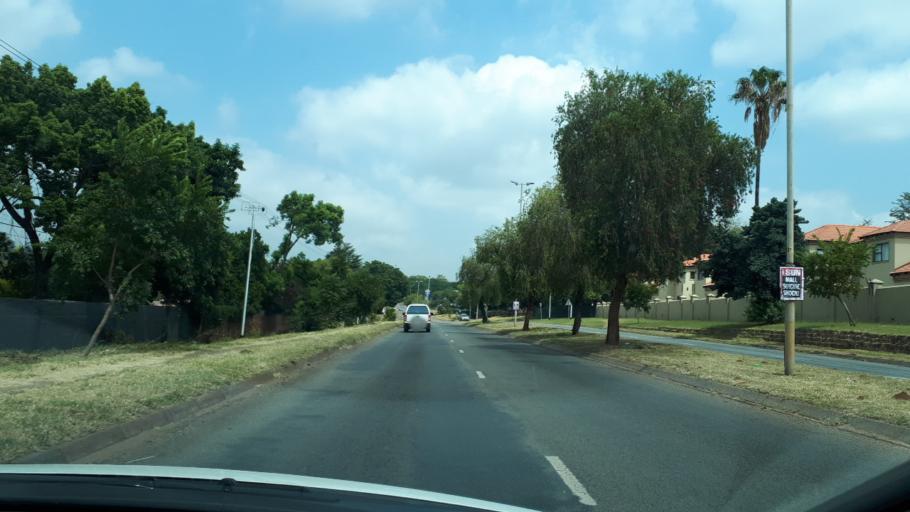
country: ZA
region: Gauteng
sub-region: City of Tshwane Metropolitan Municipality
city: Pretoria
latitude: -25.7434
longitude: 28.2988
